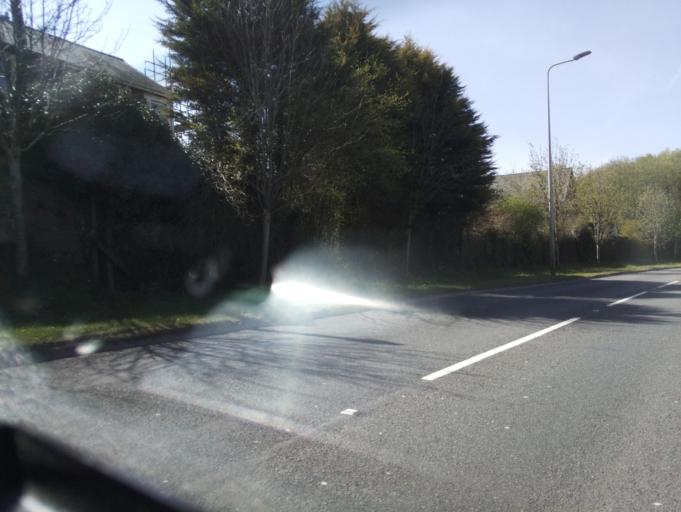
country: GB
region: Wales
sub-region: Rhondda Cynon Taf
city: Cwmbach
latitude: 51.7028
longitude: -3.4268
